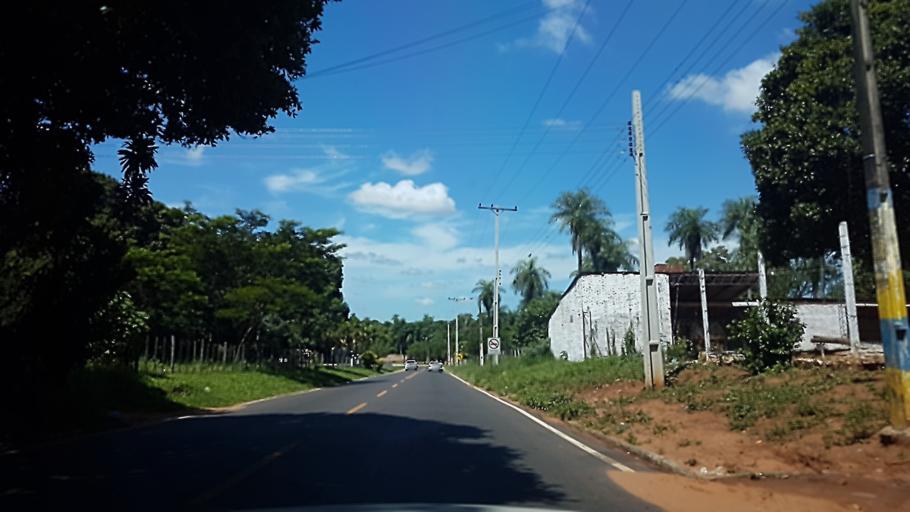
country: PY
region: Central
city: San Lorenzo
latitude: -25.3082
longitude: -57.4678
